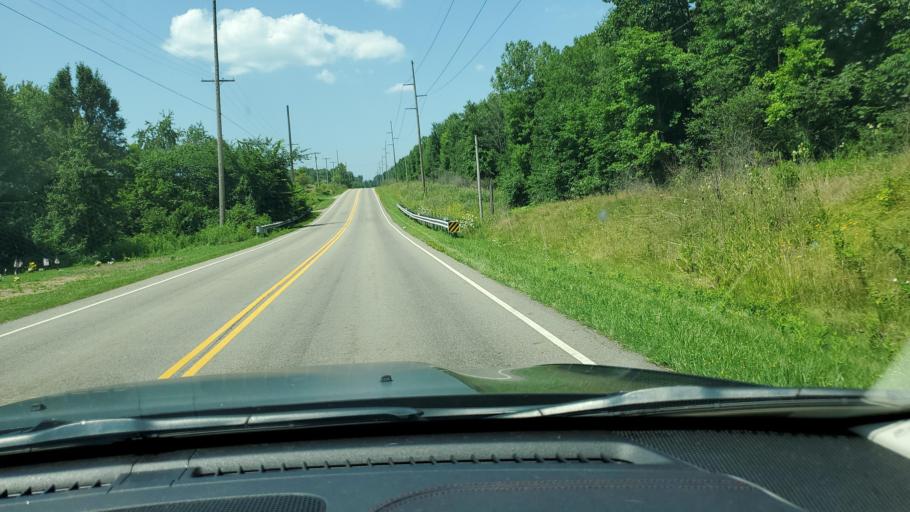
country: US
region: Ohio
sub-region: Trumbull County
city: Bolindale
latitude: 41.1932
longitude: -80.7874
